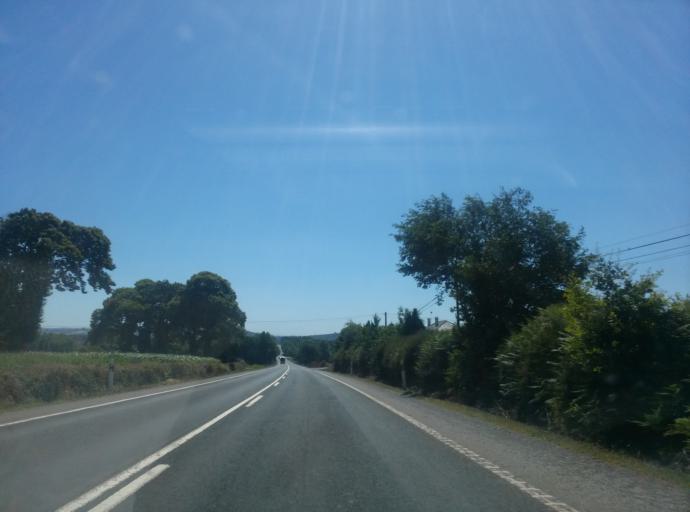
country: ES
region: Galicia
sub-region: Provincia de Lugo
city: Pol
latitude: 43.1870
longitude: -7.3457
